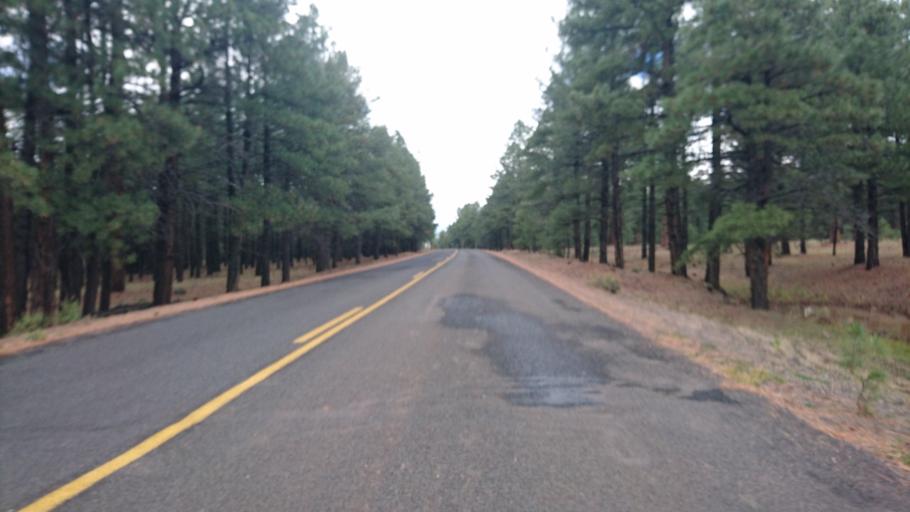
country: US
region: Arizona
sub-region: Coconino County
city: Parks
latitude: 35.2618
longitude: -111.8725
